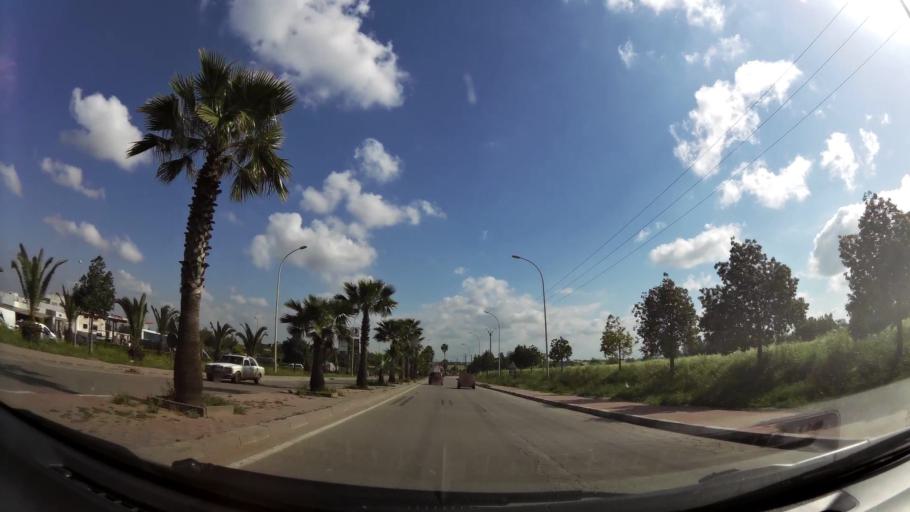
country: MA
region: Grand Casablanca
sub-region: Mediouna
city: Mediouna
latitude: 33.4547
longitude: -7.5218
